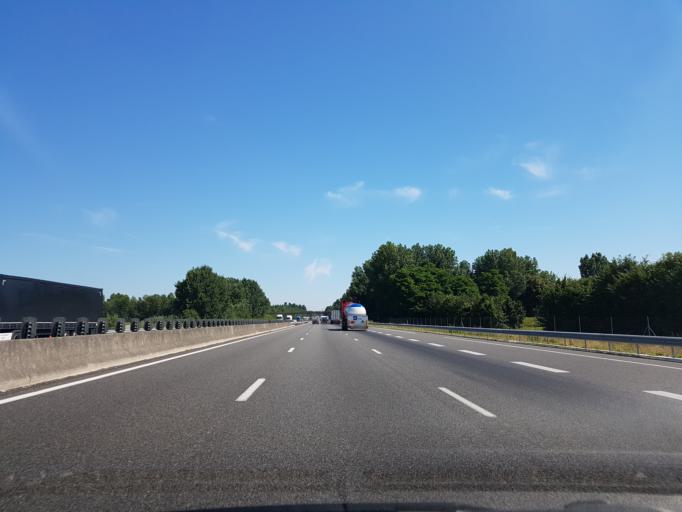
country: FR
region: Picardie
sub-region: Departement de l'Oise
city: Chevrieres
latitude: 49.3237
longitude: 2.6888
